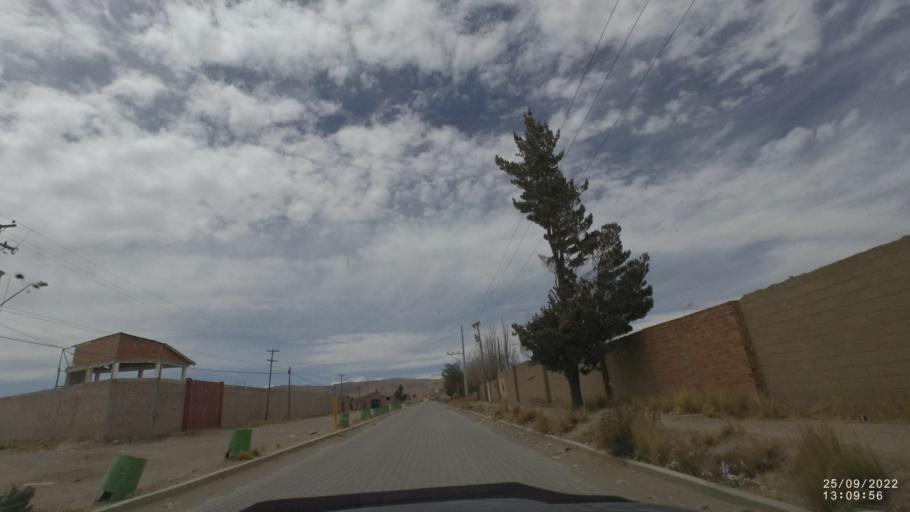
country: BO
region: Oruro
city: Oruro
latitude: -17.9739
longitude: -67.0538
